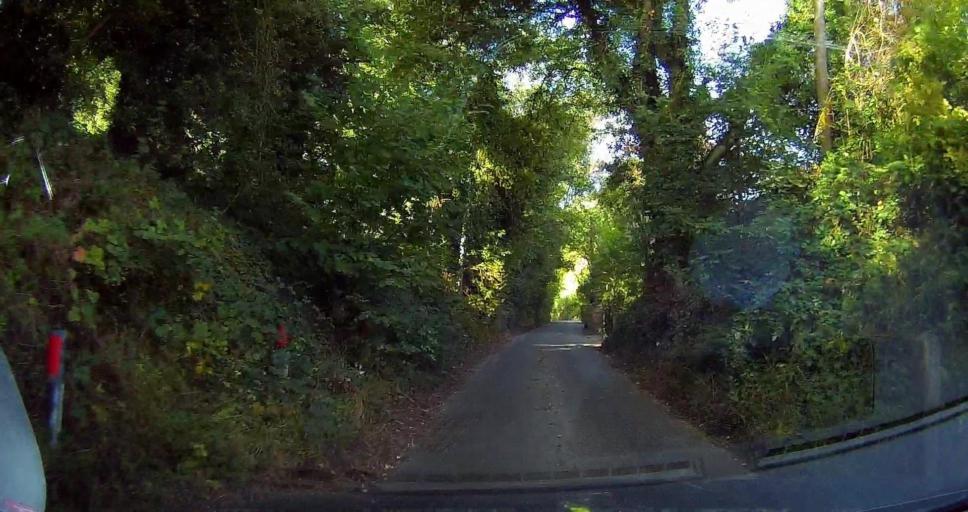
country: GB
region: England
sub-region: Kent
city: Longfield
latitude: 51.3592
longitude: 0.2865
